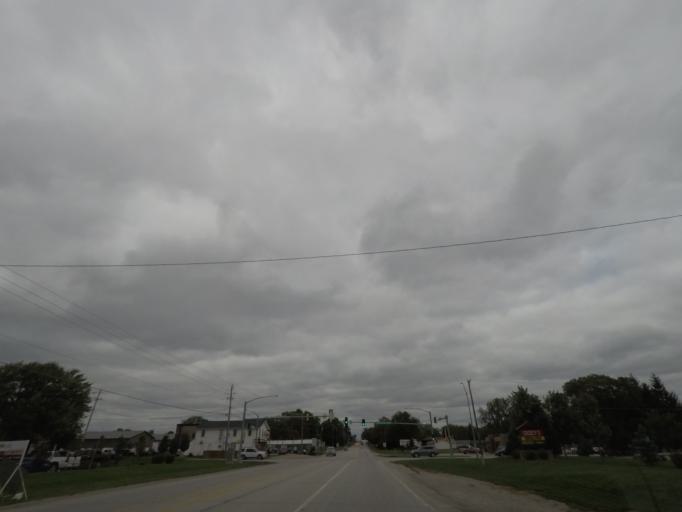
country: US
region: Iowa
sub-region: Polk County
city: Saylorville
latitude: 41.6877
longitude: -93.6005
